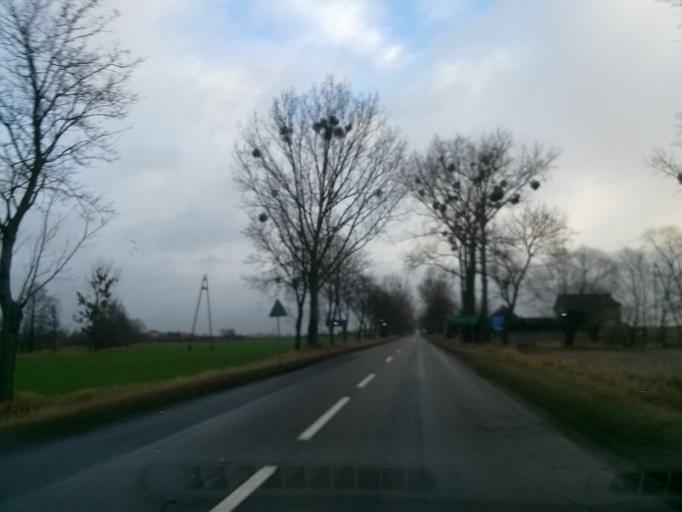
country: PL
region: Greater Poland Voivodeship
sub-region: Powiat wagrowiecki
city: Golancz
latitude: 52.8619
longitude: 17.2834
